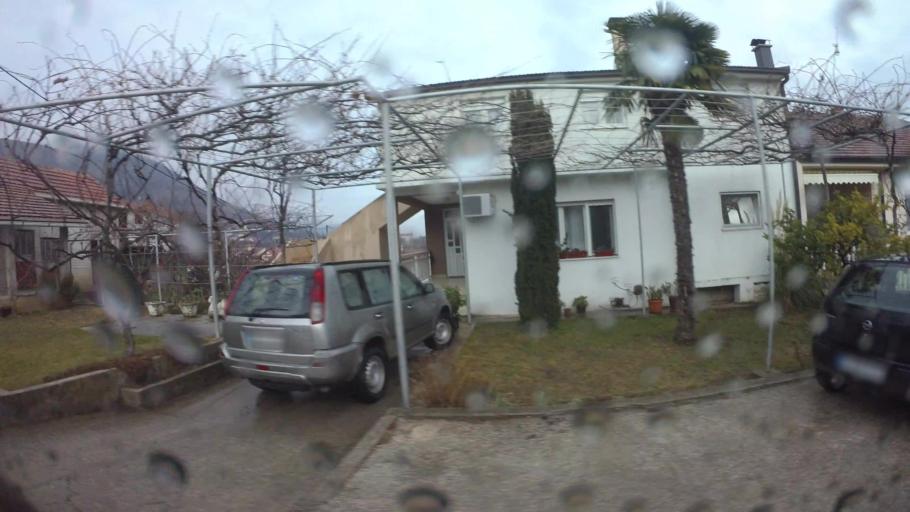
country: BA
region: Federation of Bosnia and Herzegovina
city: Cim
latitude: 43.3492
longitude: 17.7767
